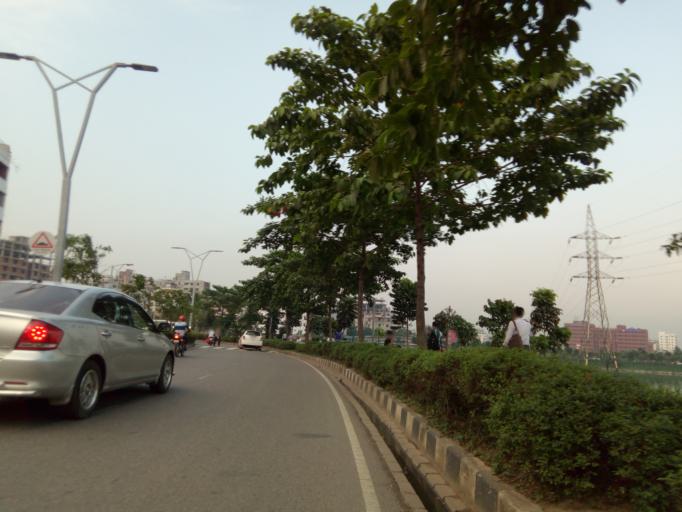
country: BD
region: Dhaka
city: Paltan
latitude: 23.7707
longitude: 90.4204
